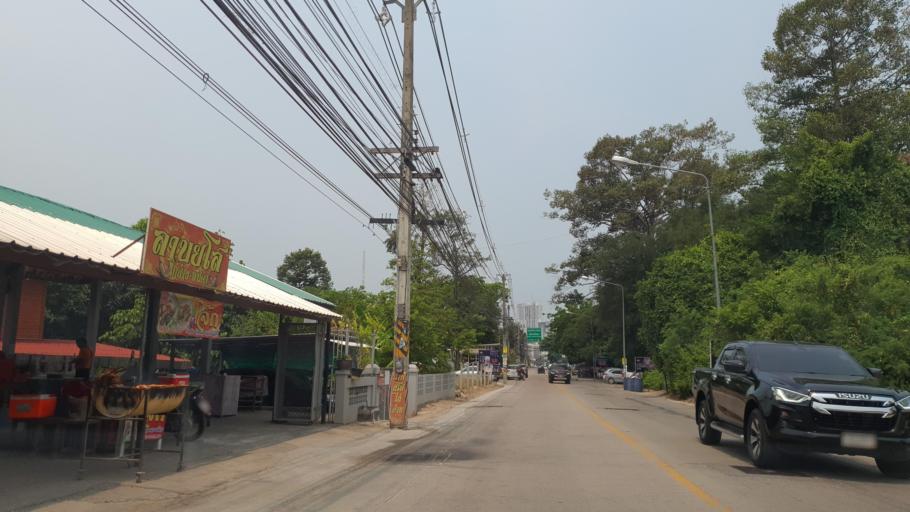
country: TH
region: Chon Buri
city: Phatthaya
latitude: 12.8898
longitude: 100.8950
